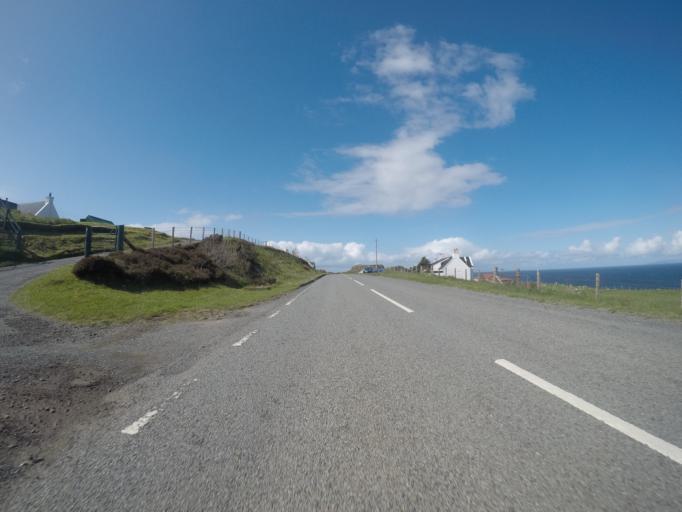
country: GB
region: Scotland
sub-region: Highland
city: Portree
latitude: 57.5951
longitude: -6.1606
